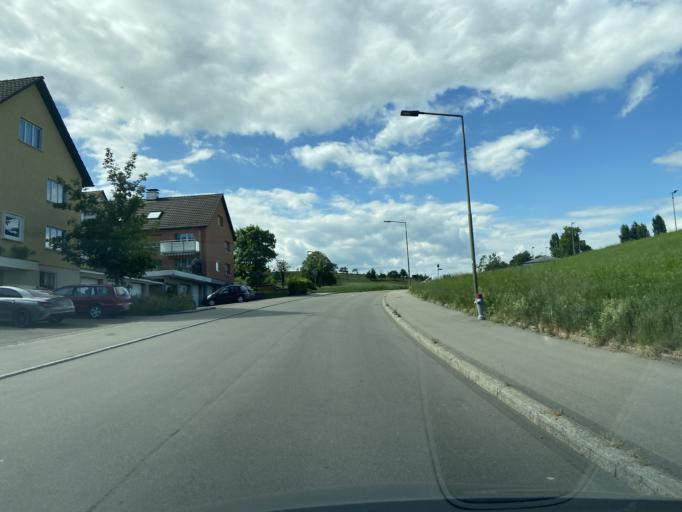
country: CH
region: Zurich
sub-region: Bezirk Winterthur
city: Wuelflingen (Kreis 6) / Lindenplatz
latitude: 47.5173
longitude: 8.6905
